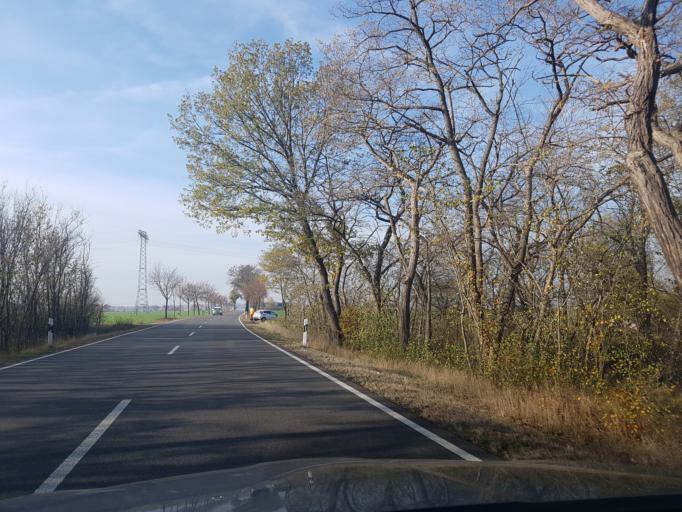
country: DE
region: Saxony
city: Beilrode
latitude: 51.5503
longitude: 13.0939
